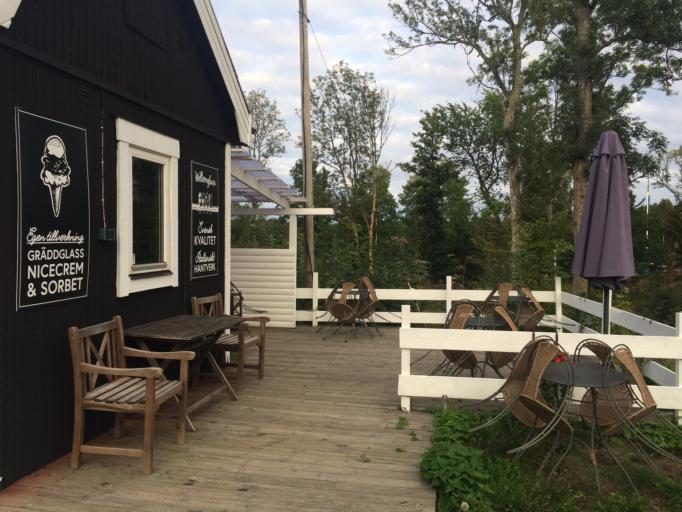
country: SE
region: Vaestra Goetaland
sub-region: Karlsborgs Kommun
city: Karlsborg
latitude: 58.5761
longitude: 14.4351
